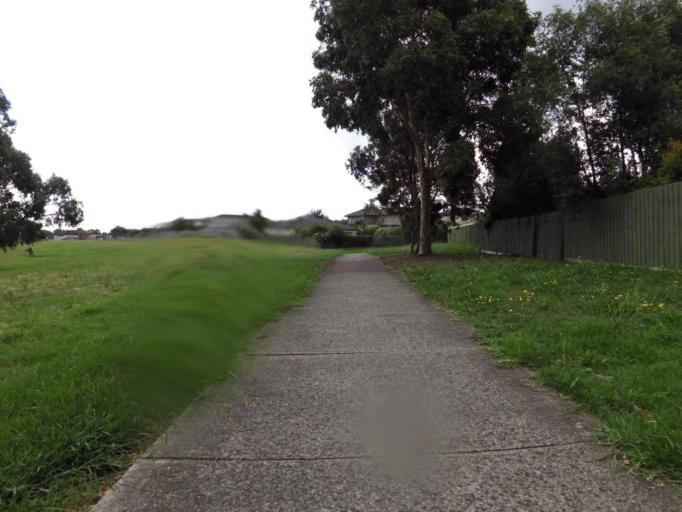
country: AU
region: Victoria
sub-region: Knox
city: Knoxfield
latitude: -37.9095
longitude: 145.2732
